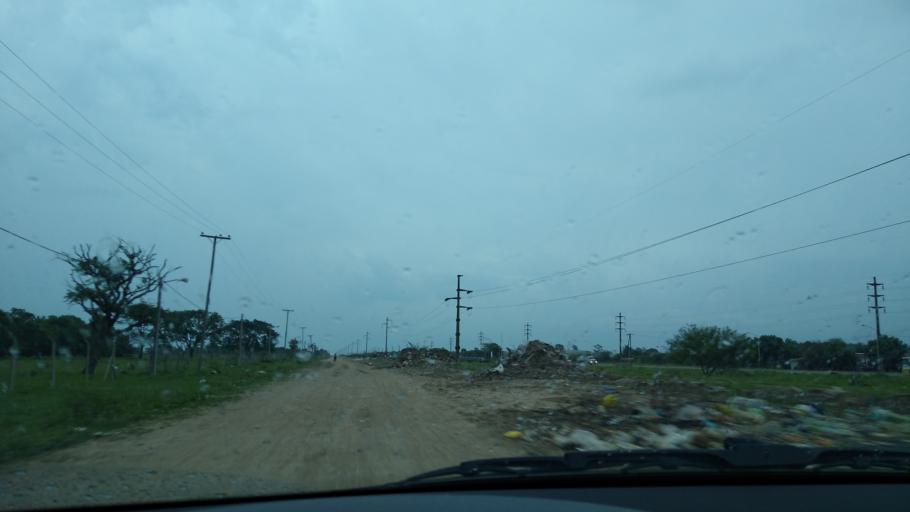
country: AR
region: Chaco
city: Resistencia
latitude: -27.4984
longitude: -58.9778
